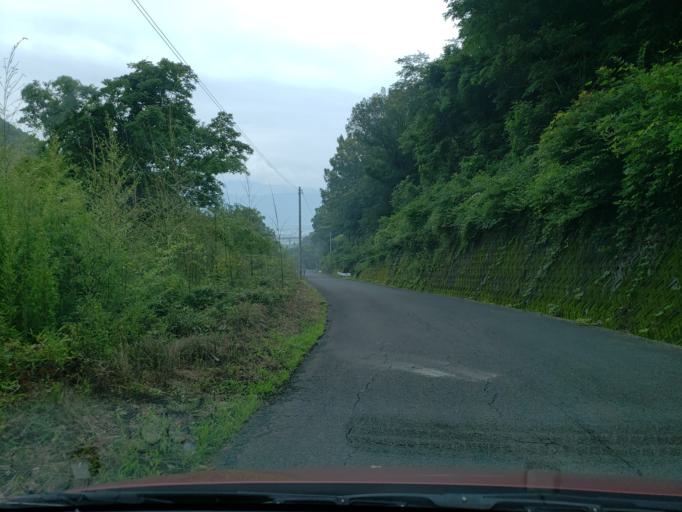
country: JP
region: Tokushima
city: Kamojimacho-jogejima
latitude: 34.1113
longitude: 134.2989
